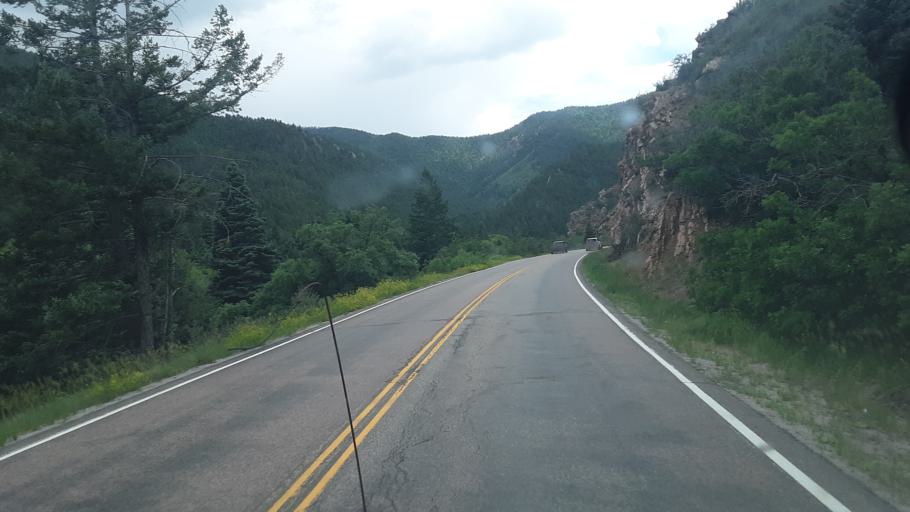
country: US
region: Colorado
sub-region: Fremont County
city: Florence
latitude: 38.1737
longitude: -105.1544
